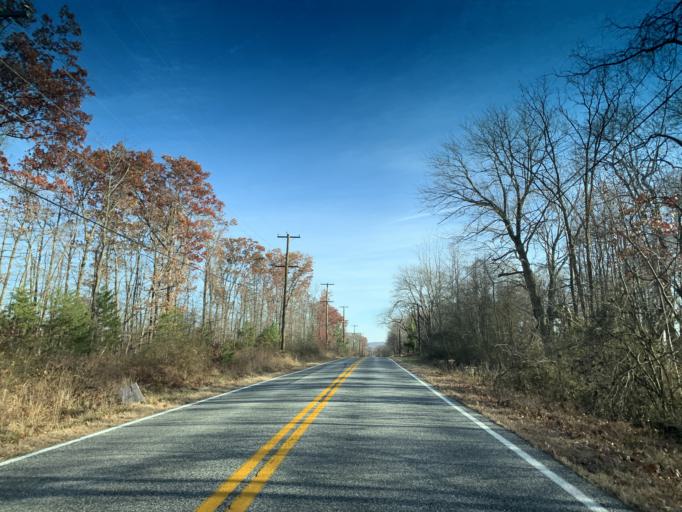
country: US
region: Maryland
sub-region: Cecil County
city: Charlestown
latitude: 39.5828
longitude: -76.0086
